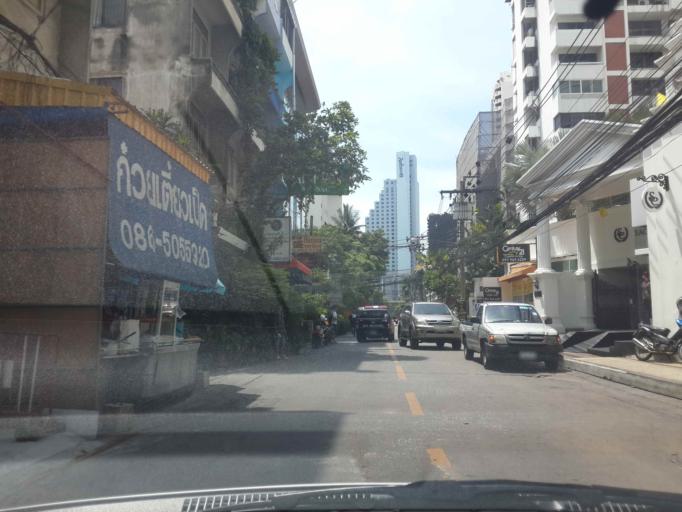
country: TH
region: Bangkok
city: Khlong Toei
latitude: 13.7305
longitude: 100.5639
